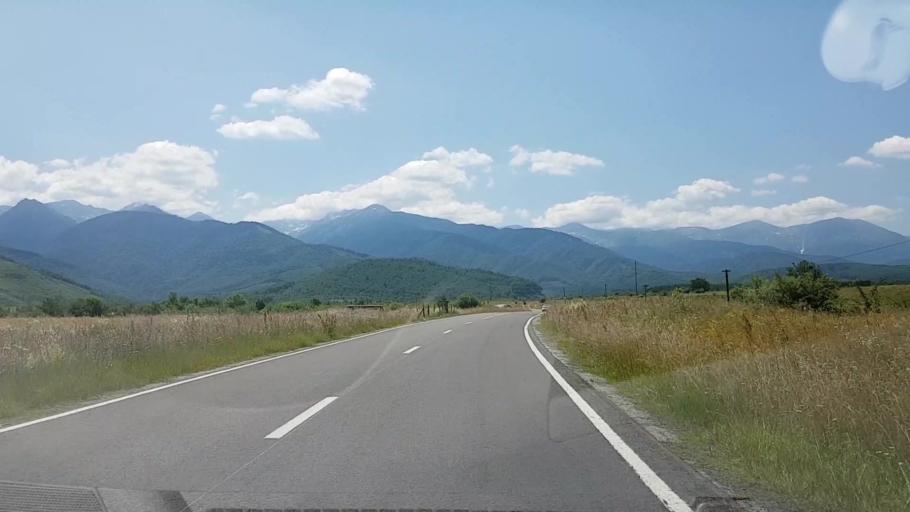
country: RO
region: Sibiu
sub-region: Comuna Cartisoara
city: Cartisoara
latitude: 45.7137
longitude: 24.5690
